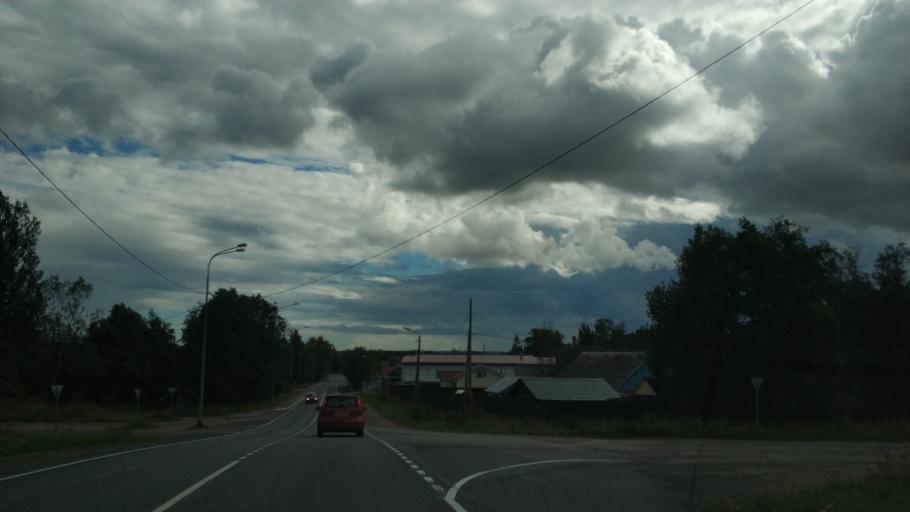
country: RU
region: Republic of Karelia
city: Khelyulya
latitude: 61.7537
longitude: 30.6585
